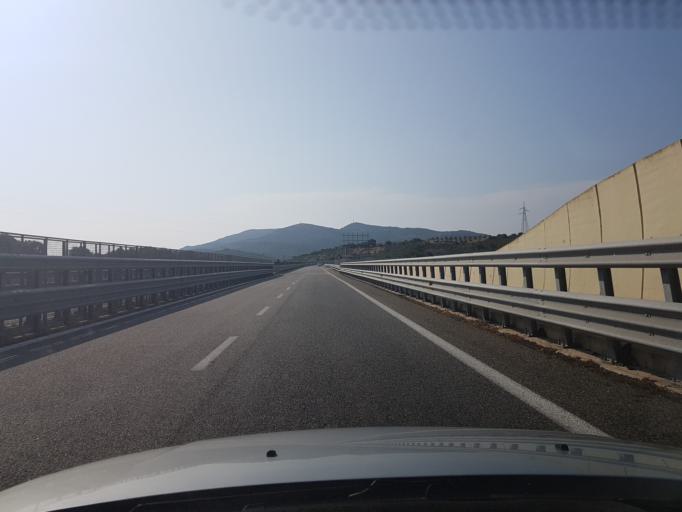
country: IT
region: Sardinia
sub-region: Provincia di Olbia-Tempio
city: San Teodoro
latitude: 40.7668
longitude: 9.6407
